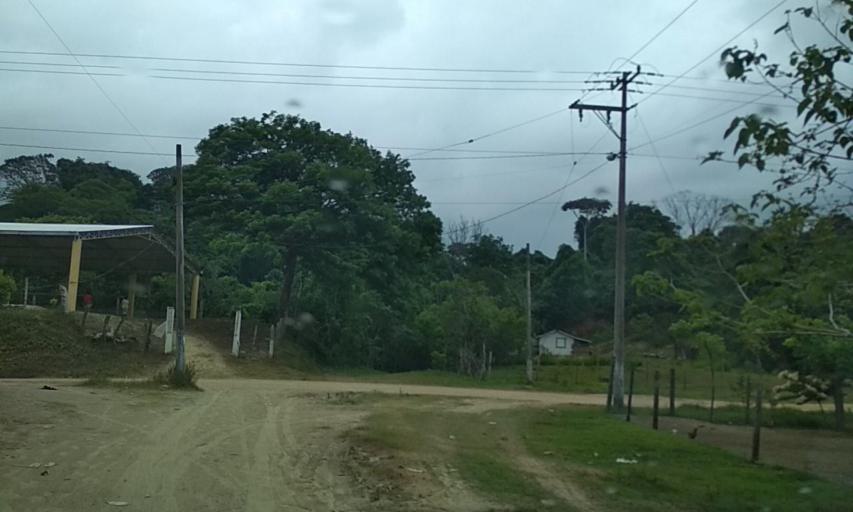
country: MX
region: Tabasco
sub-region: Huimanguillo
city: Francisco Rueda
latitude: 17.6550
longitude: -94.0990
